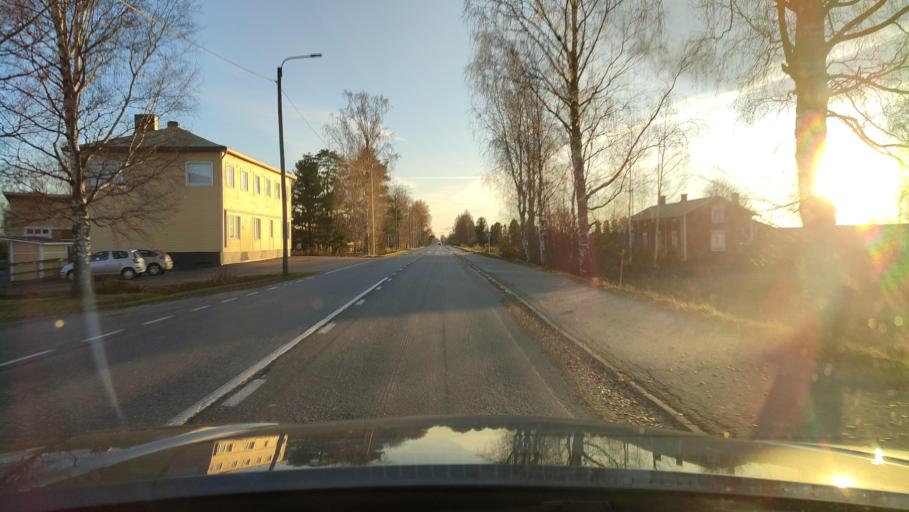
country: FI
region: Ostrobothnia
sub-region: Sydosterbotten
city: Naerpes
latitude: 62.5435
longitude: 21.3950
